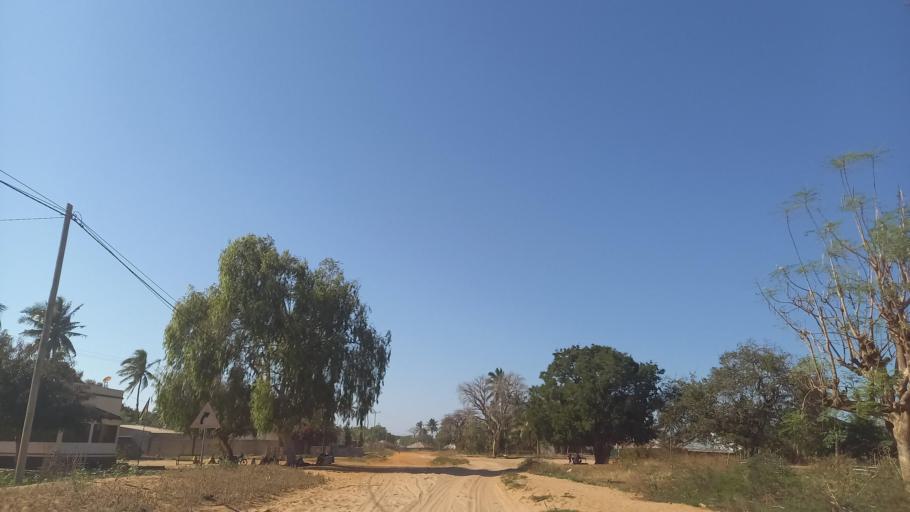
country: MZ
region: Cabo Delgado
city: Pemba
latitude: -13.1425
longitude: 40.5545
